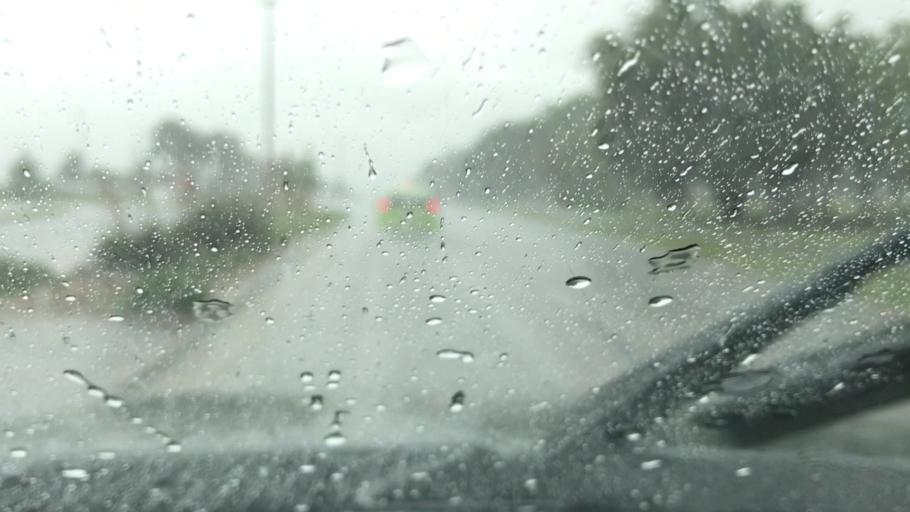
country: US
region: Texas
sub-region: Williamson County
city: Leander
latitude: 30.5425
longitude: -97.8634
